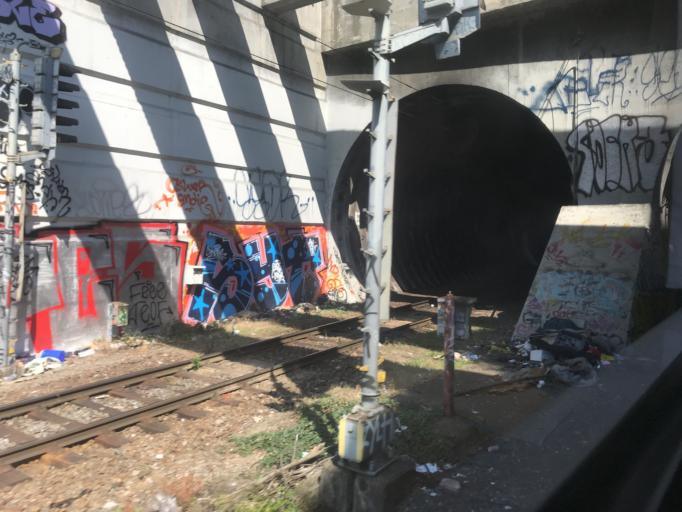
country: CZ
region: Praha
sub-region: Praha 2
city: Vysehrad
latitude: 50.0693
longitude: 14.4368
